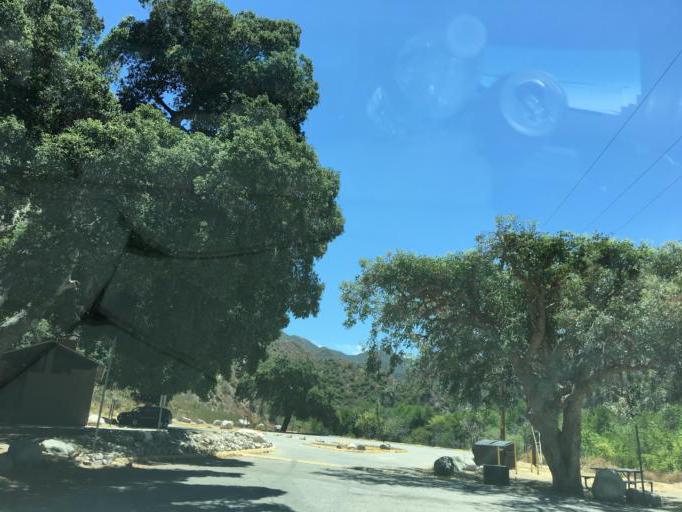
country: US
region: California
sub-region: Los Angeles County
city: La Crescenta-Montrose
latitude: 34.2853
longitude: -118.2242
